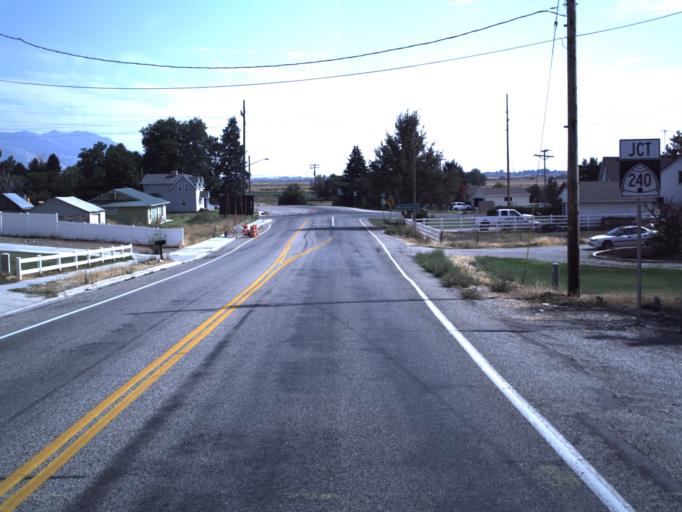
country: US
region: Utah
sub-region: Box Elder County
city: Honeyville
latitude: 41.6361
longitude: -112.0796
